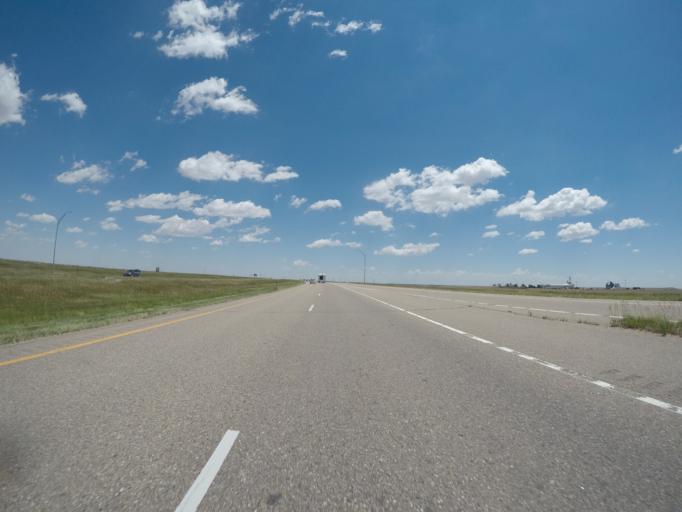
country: US
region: Colorado
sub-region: Lincoln County
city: Hugo
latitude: 39.2751
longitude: -103.4870
